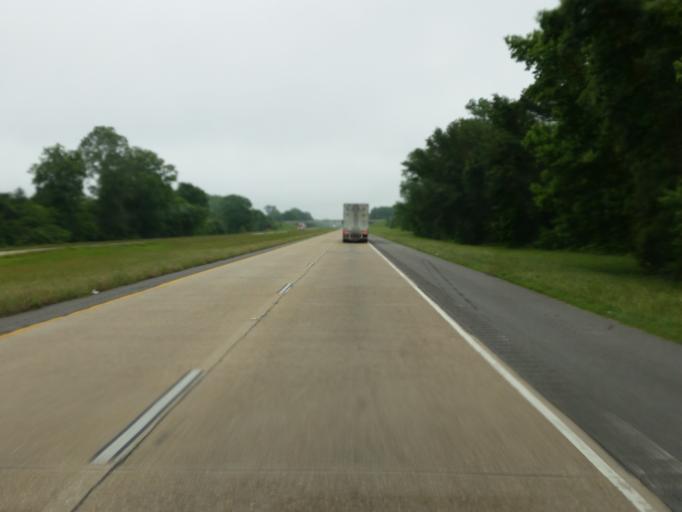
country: US
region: Louisiana
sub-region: Madison Parish
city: Tallulah
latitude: 32.3692
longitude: -91.1369
